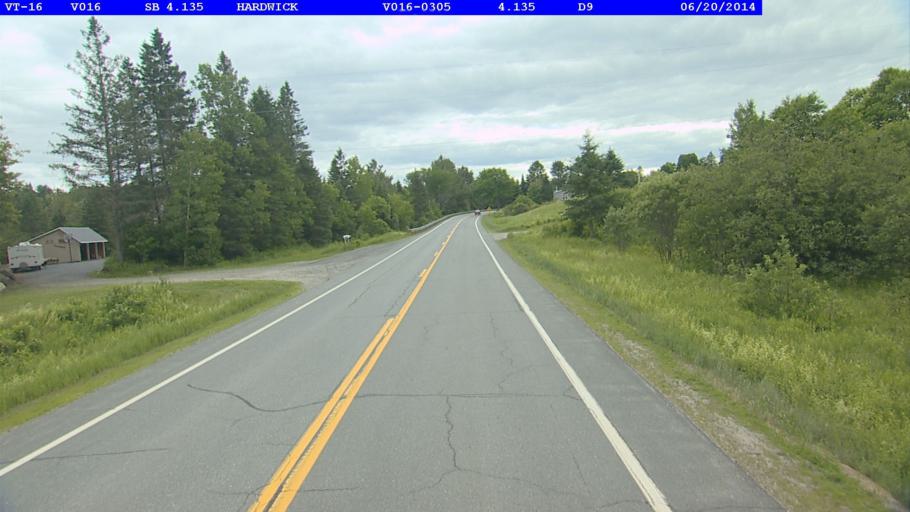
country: US
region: Vermont
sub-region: Caledonia County
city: Hardwick
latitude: 44.5406
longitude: -72.2700
